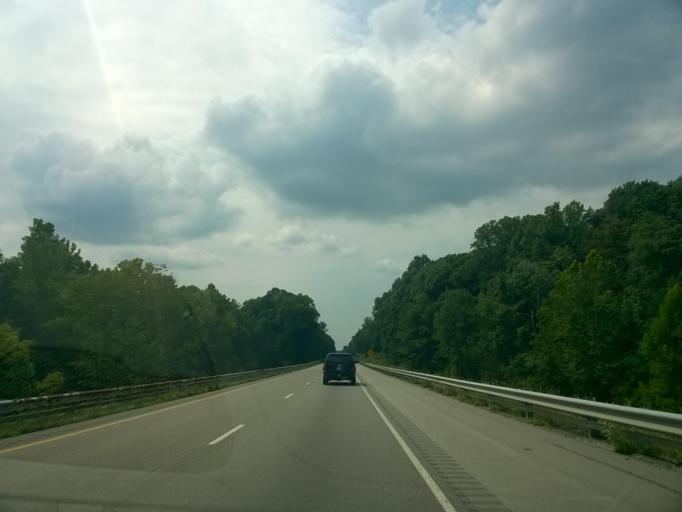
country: US
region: Indiana
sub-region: Putnam County
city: Cloverdale
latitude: 39.5217
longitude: -86.8972
